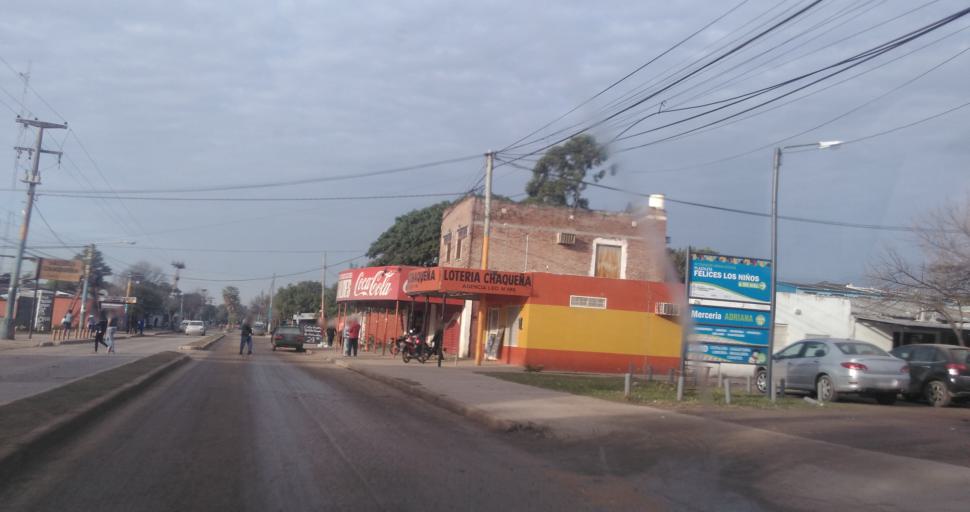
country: AR
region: Chaco
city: Resistencia
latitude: -27.4826
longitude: -58.9894
